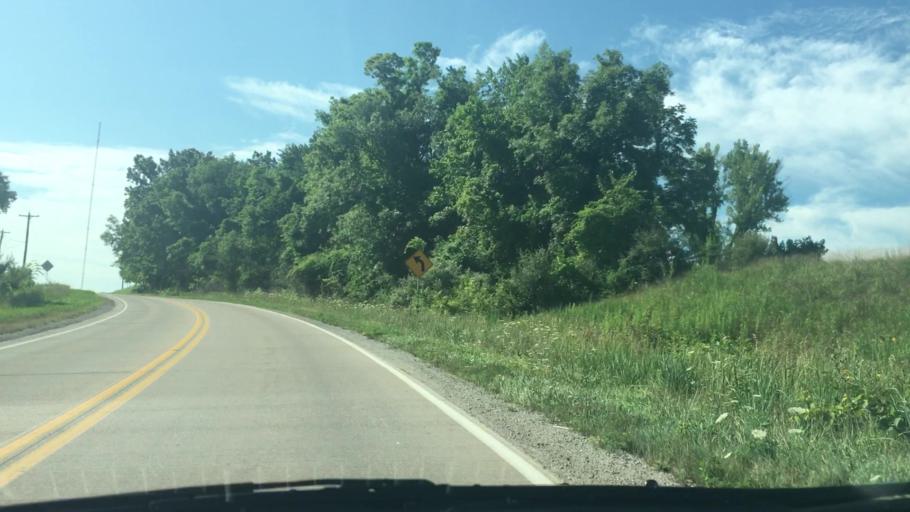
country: US
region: Iowa
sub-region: Johnson County
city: Iowa City
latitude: 41.6915
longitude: -91.5470
